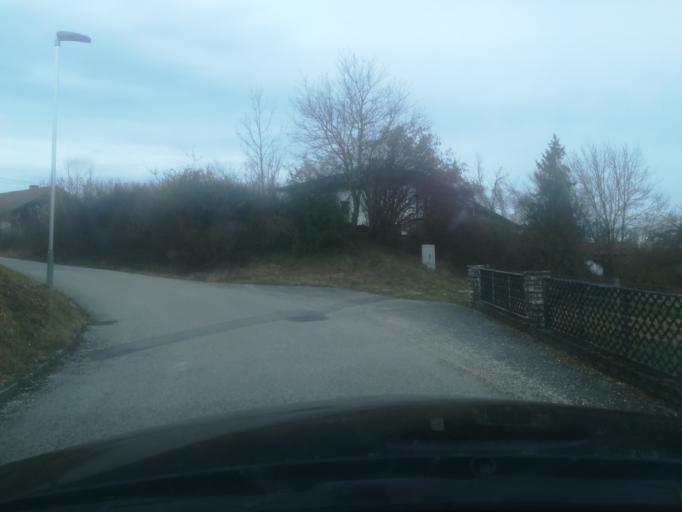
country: AT
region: Upper Austria
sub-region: Wels-Land
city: Bad Wimsbach-Neydharting
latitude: 48.0931
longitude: 13.9073
